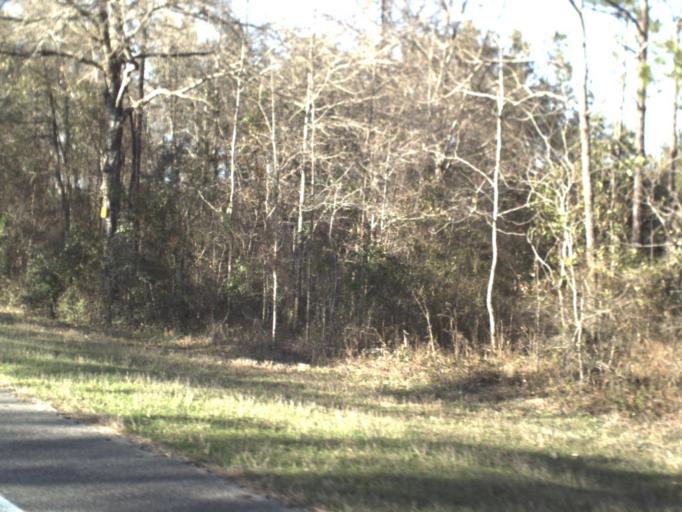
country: US
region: Florida
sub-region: Jackson County
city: Marianna
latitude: 30.6307
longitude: -85.1849
